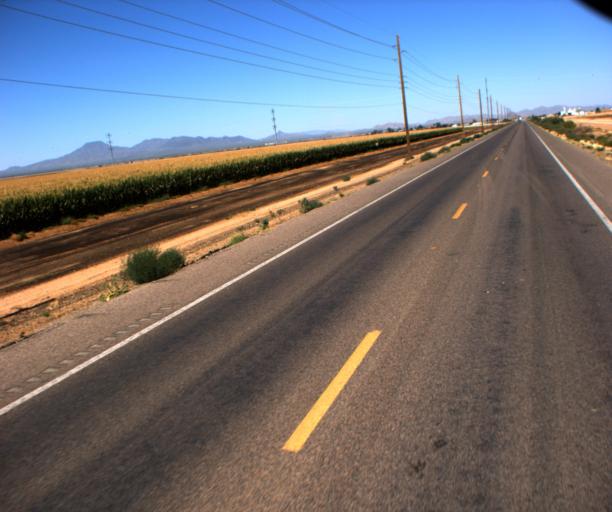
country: US
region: Arizona
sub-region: Pinal County
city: Casa Grande
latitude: 32.8794
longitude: -111.9380
